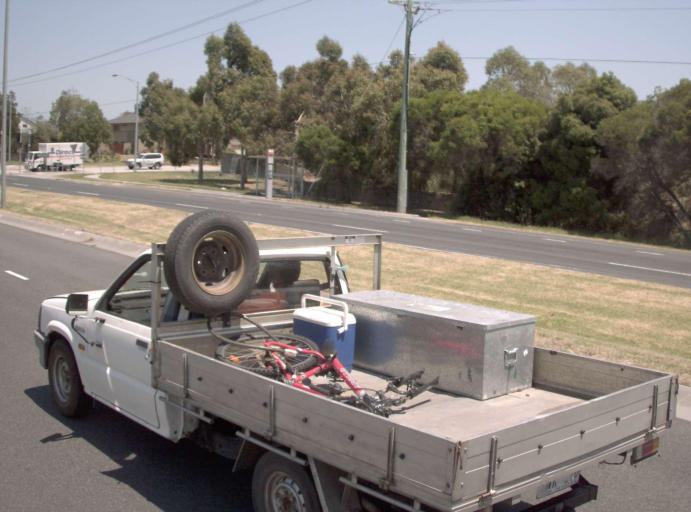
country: AU
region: Victoria
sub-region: Kingston
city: Waterways
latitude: -38.0153
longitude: 145.1400
